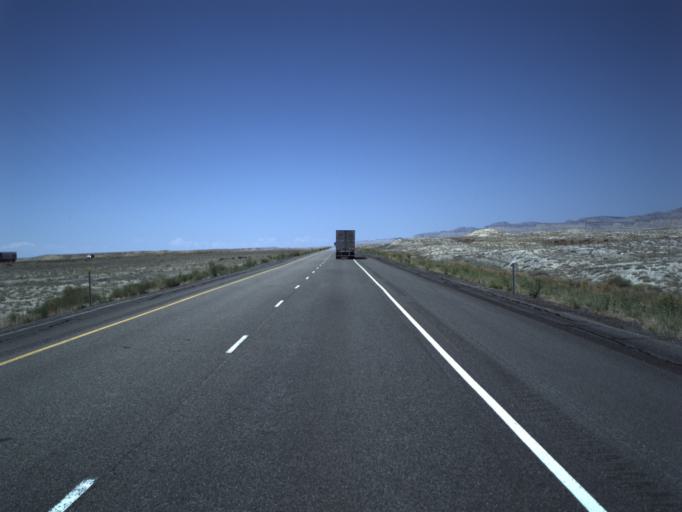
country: US
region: Utah
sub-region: Grand County
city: Moab
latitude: 38.9363
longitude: -109.4663
